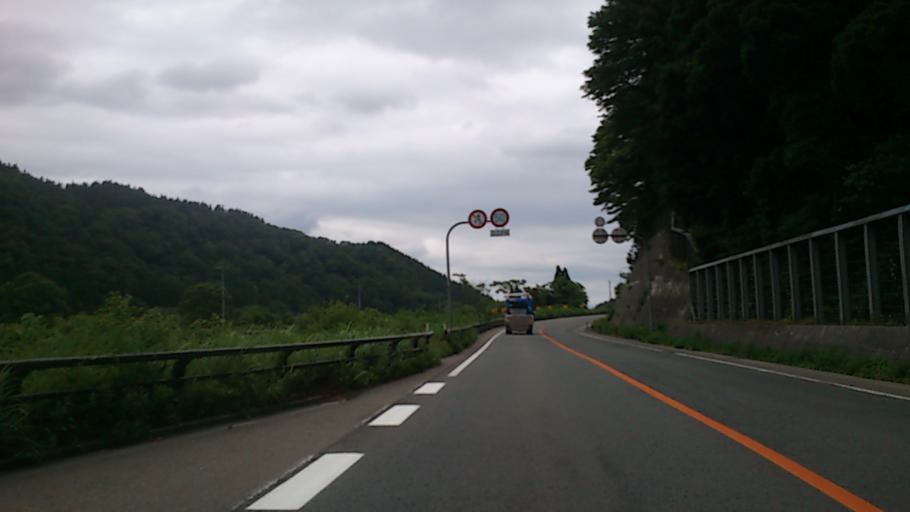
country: JP
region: Yamagata
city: Shinjo
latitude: 38.7444
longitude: 140.1207
